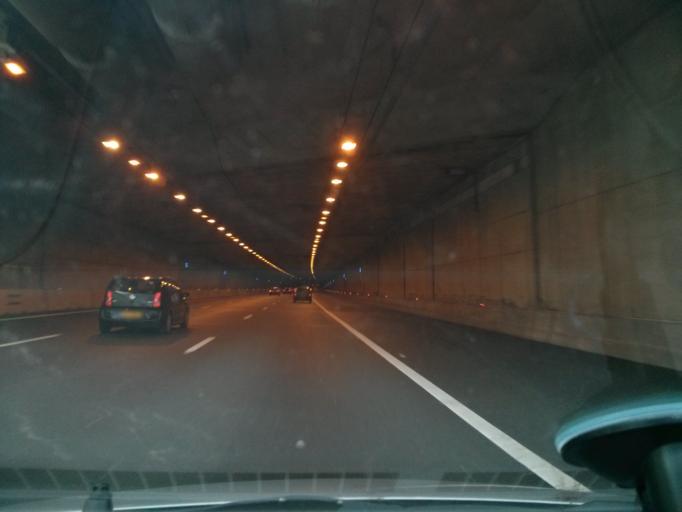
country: NL
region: Utrecht
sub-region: Stichtse Vecht
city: Maarssen
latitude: 52.0995
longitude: 5.0666
